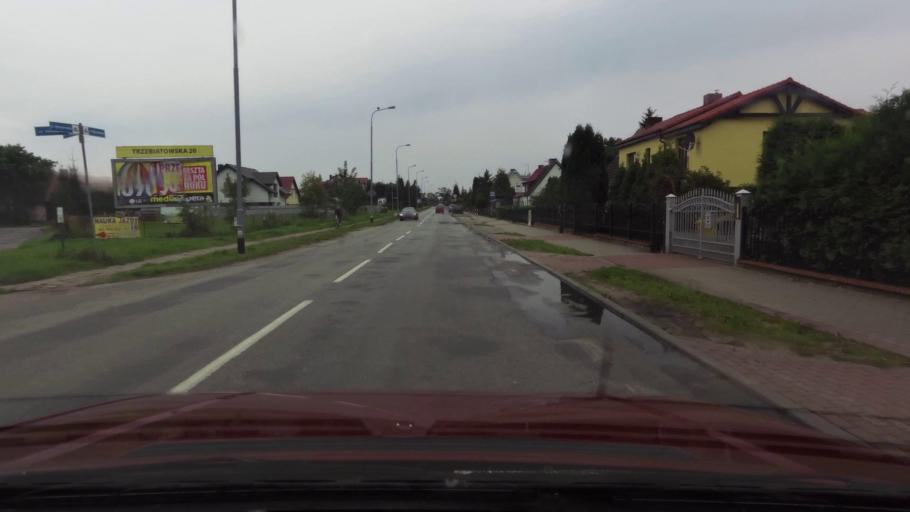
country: PL
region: West Pomeranian Voivodeship
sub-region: Powiat kolobrzeski
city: Kolobrzeg
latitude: 54.1597
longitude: 15.5478
